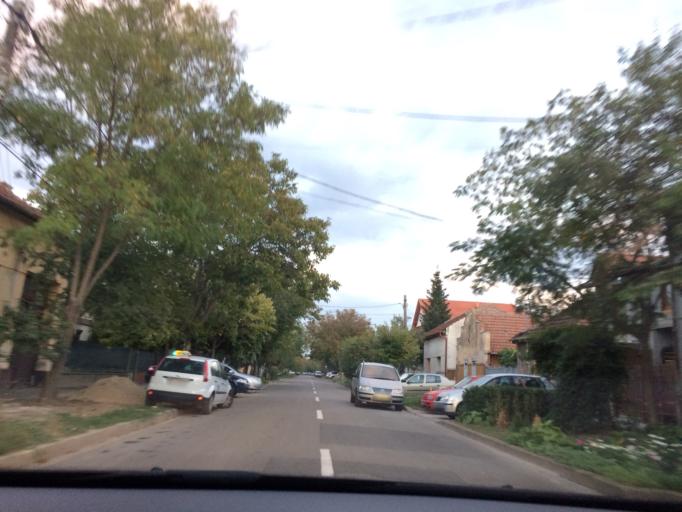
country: RO
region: Timis
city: Timisoara
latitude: 45.7626
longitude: 21.1975
